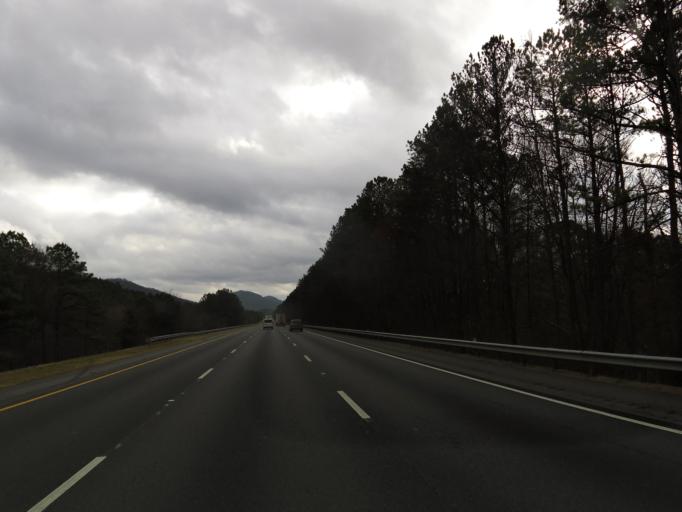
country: US
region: Georgia
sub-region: Whitfield County
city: Varnell
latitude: 34.8358
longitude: -85.0181
